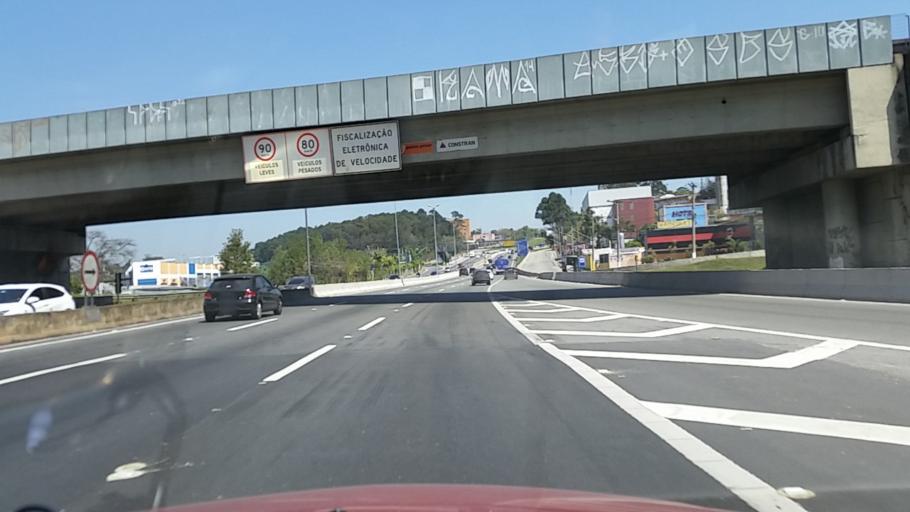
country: BR
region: Sao Paulo
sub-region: Taboao Da Serra
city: Taboao da Serra
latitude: -23.5909
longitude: -46.7982
